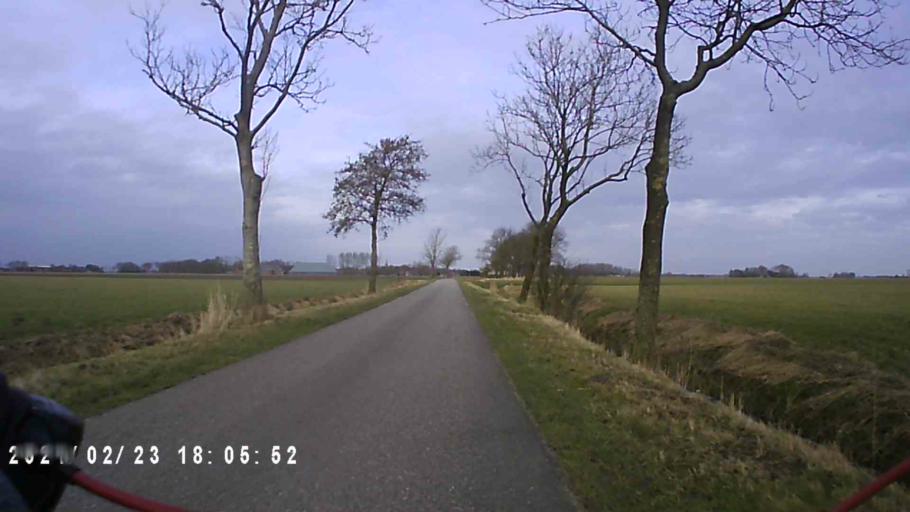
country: NL
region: Groningen
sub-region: Gemeente Bedum
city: Bedum
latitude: 53.3942
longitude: 6.5990
